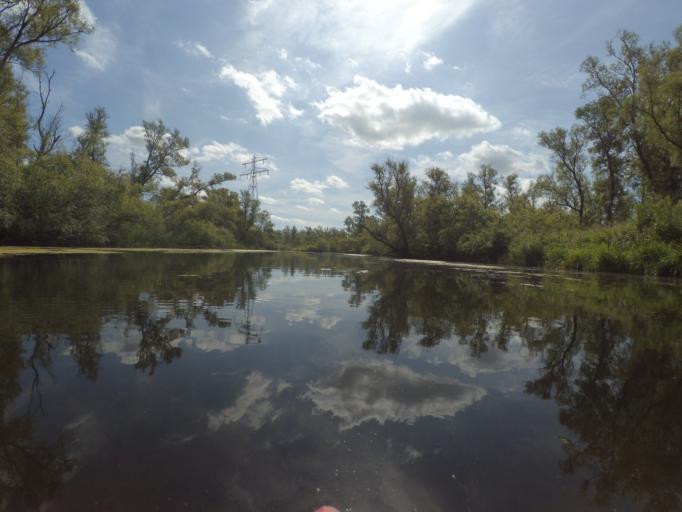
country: NL
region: North Brabant
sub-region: Gemeente Made en Drimmelen
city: Drimmelen
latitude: 51.7488
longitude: 4.8065
